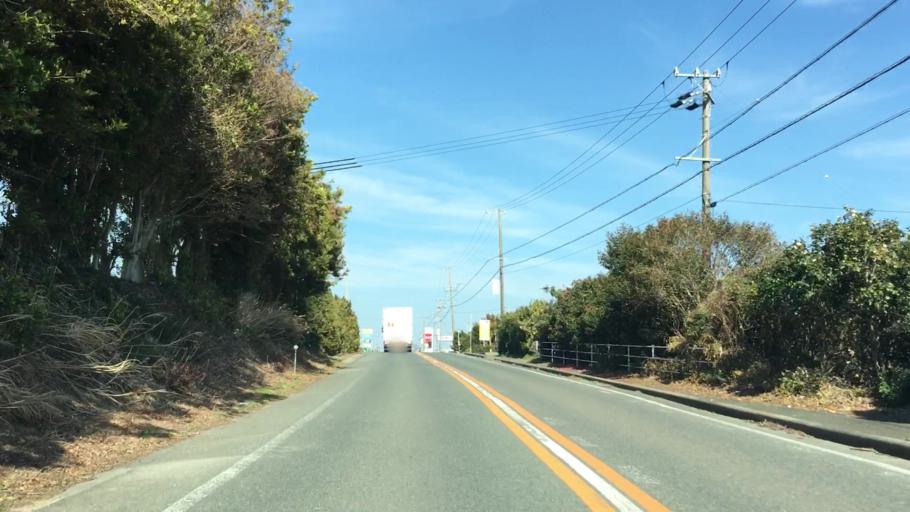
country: JP
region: Shizuoka
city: Kosai-shi
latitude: 34.6820
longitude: 137.4477
